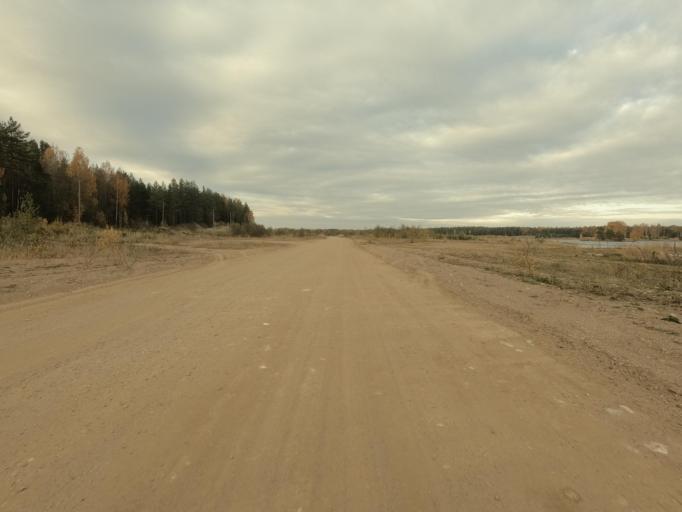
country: RU
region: Leningrad
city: Priladozhskiy
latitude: 59.7025
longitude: 31.3629
